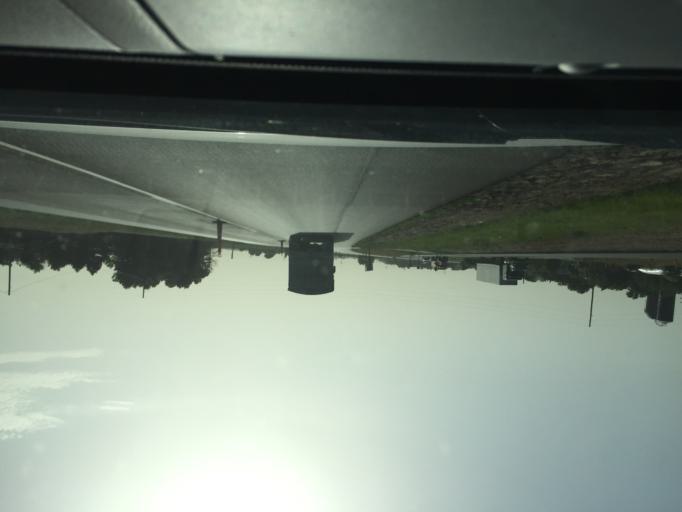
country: US
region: Kansas
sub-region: Reno County
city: South Hutchinson
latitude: 38.0144
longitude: -97.9942
